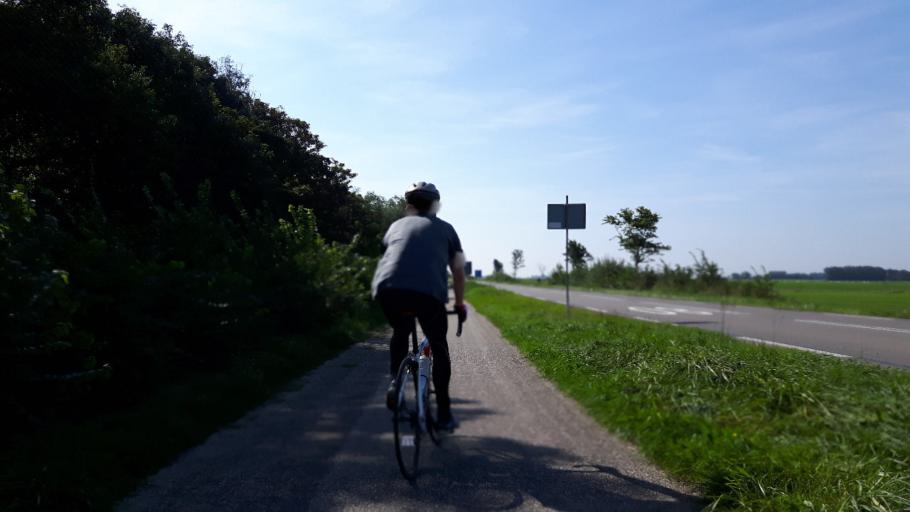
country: NL
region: Friesland
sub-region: Gemeente Dongeradeel
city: Holwerd
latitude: 53.3718
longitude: 5.8954
